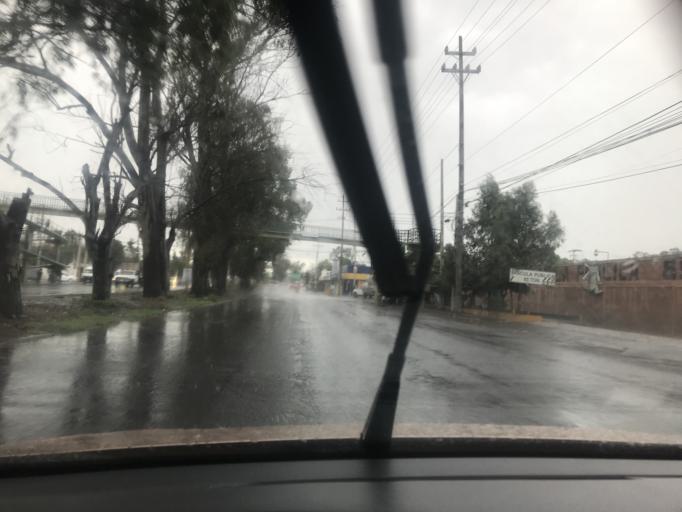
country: MX
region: Mexico
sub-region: Texcoco
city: Santa Martha
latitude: 19.4289
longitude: -98.9091
